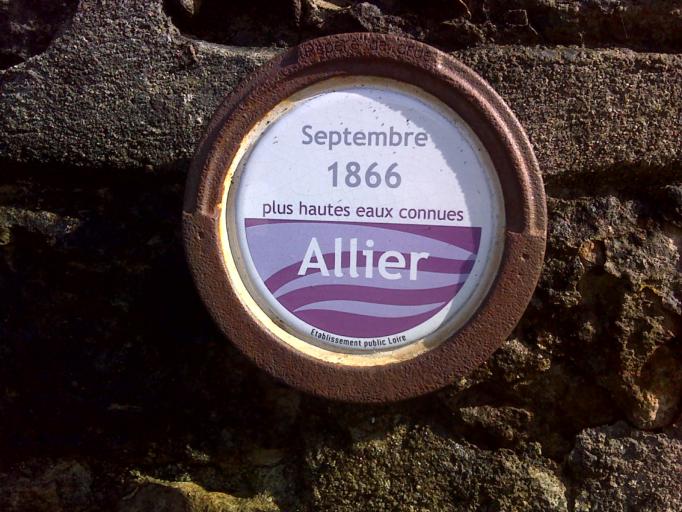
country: FR
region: Centre
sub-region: Departement du Cher
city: Cuffy
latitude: 46.9479
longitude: 3.0704
